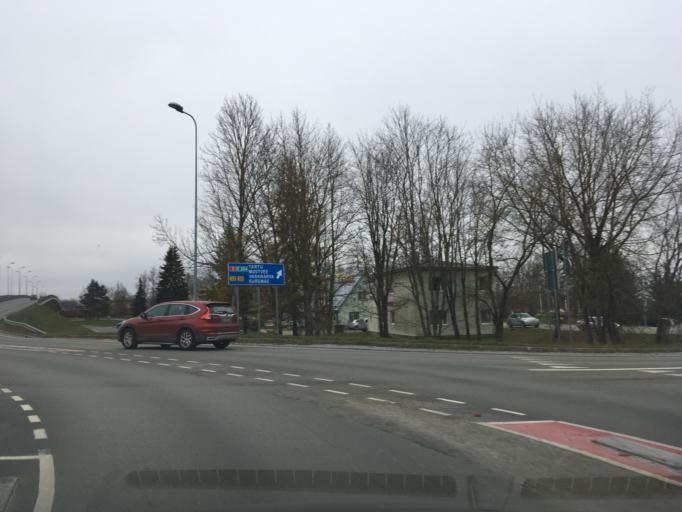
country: EE
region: Ida-Virumaa
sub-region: Johvi vald
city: Johvi
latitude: 59.3577
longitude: 27.4104
